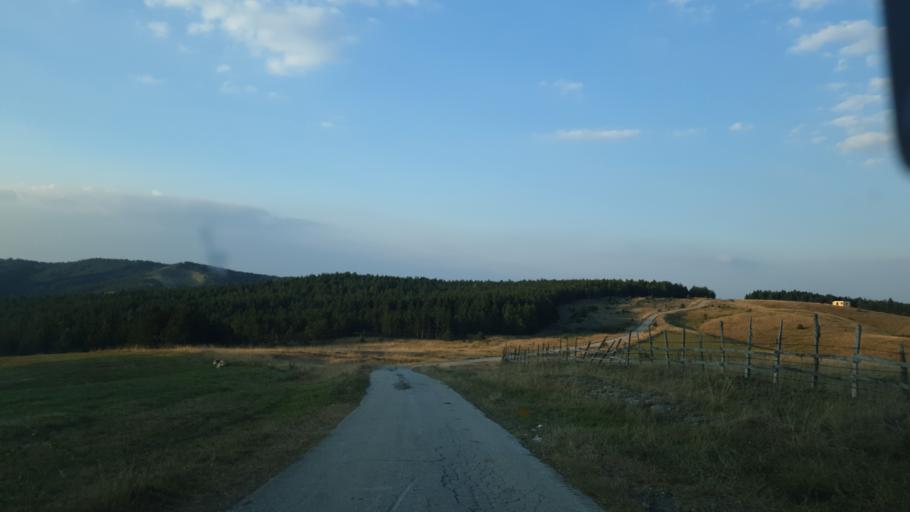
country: RS
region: Central Serbia
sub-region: Zlatiborski Okrug
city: Kosjeric
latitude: 44.0156
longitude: 19.9980
